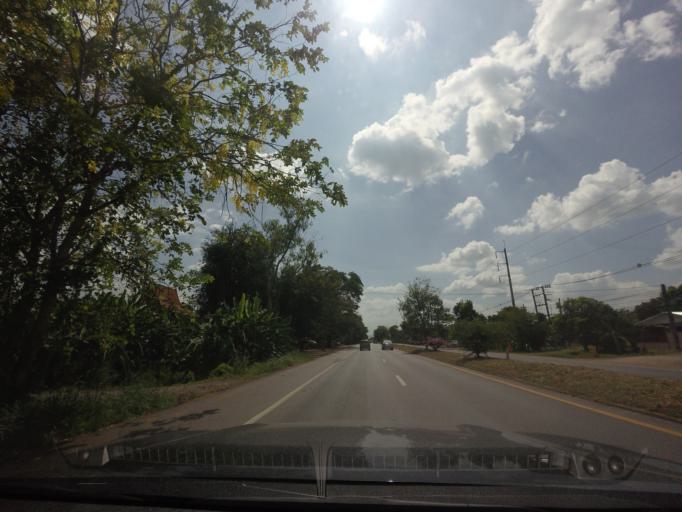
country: TH
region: Phetchabun
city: Nong Phai
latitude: 15.9561
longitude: 101.0425
